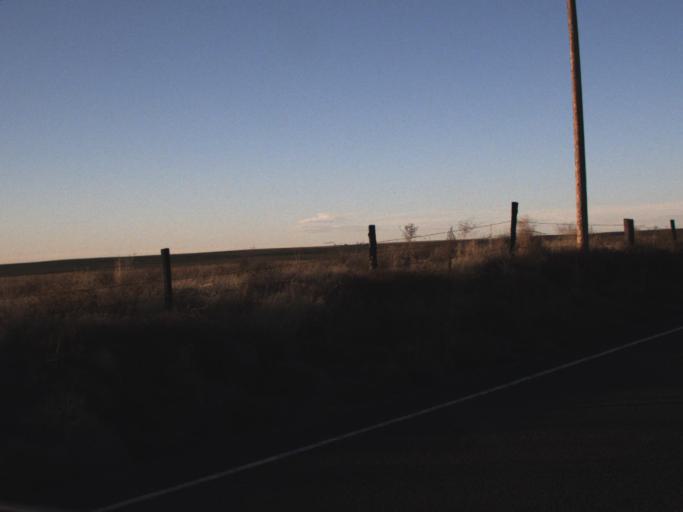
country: US
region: Washington
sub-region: Franklin County
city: Connell
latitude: 46.7830
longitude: -118.5473
